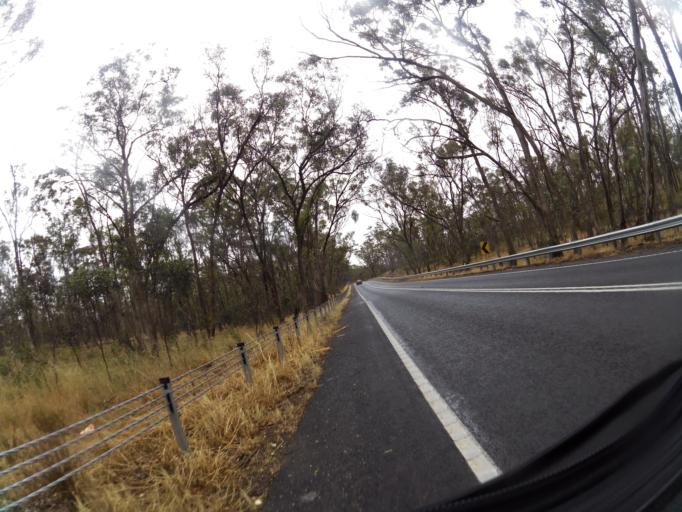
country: AU
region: Victoria
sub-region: Mount Alexander
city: Castlemaine
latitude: -37.1028
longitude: 144.1071
